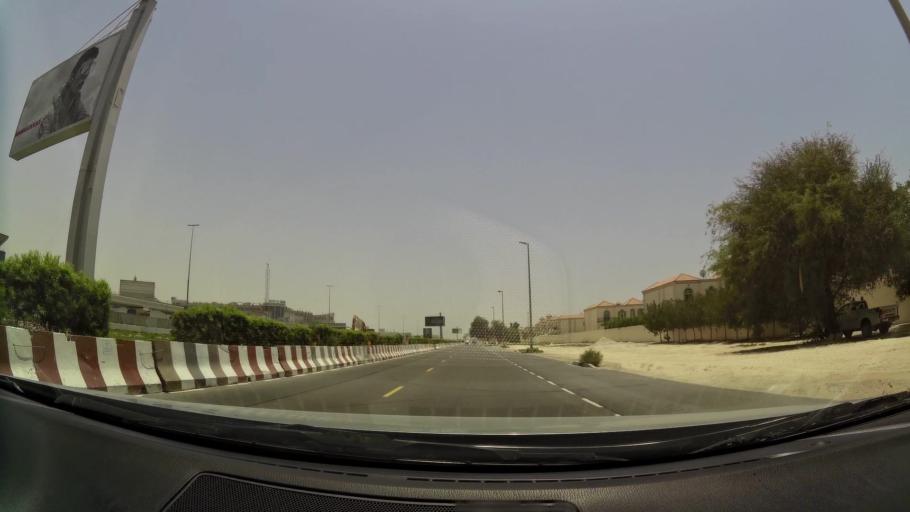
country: AE
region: Dubai
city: Dubai
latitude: 25.1738
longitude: 55.2428
